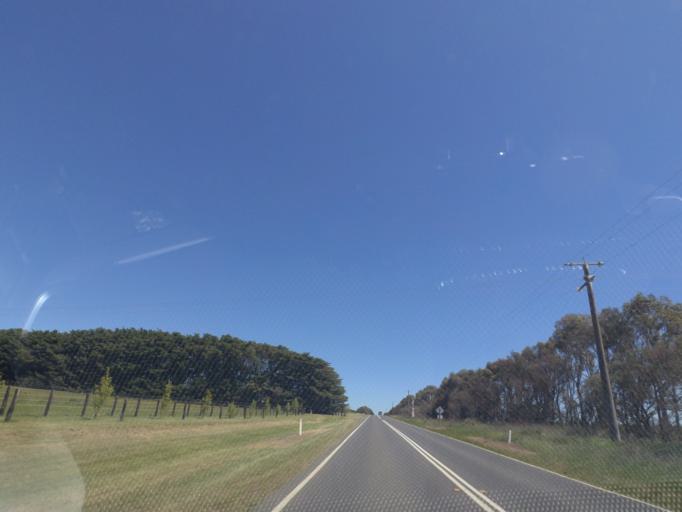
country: AU
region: Victoria
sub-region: Hume
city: Sunbury
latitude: -37.2850
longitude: 144.7722
